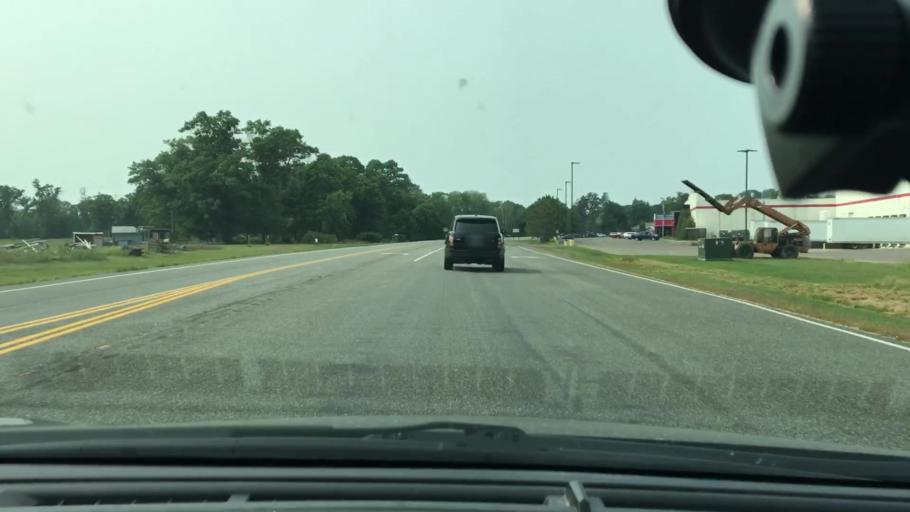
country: US
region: Minnesota
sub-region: Crow Wing County
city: Breezy Point
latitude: 46.4884
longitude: -94.1558
